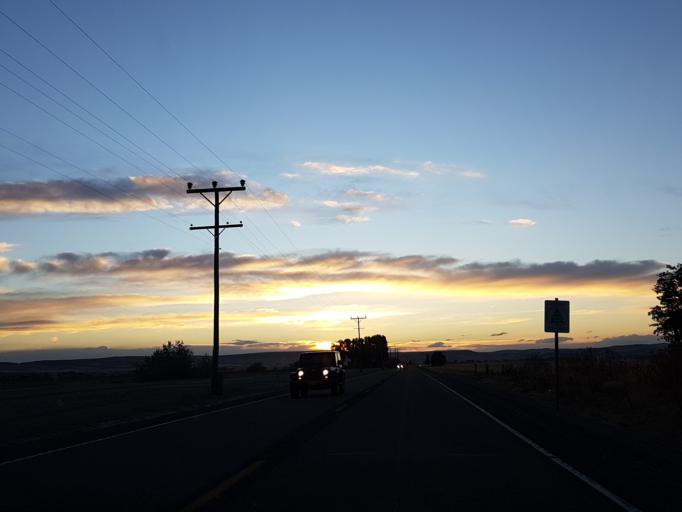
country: US
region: Oregon
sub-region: Malheur County
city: Vale
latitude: 43.9391
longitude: -117.3379
